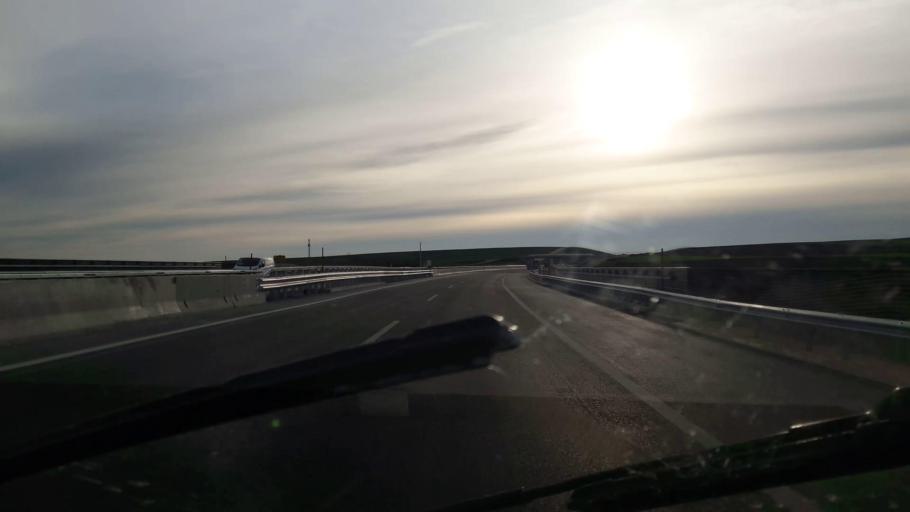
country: AT
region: Lower Austria
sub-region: Politischer Bezirk Mistelbach
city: Wilfersdorf
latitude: 48.6141
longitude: 16.6755
